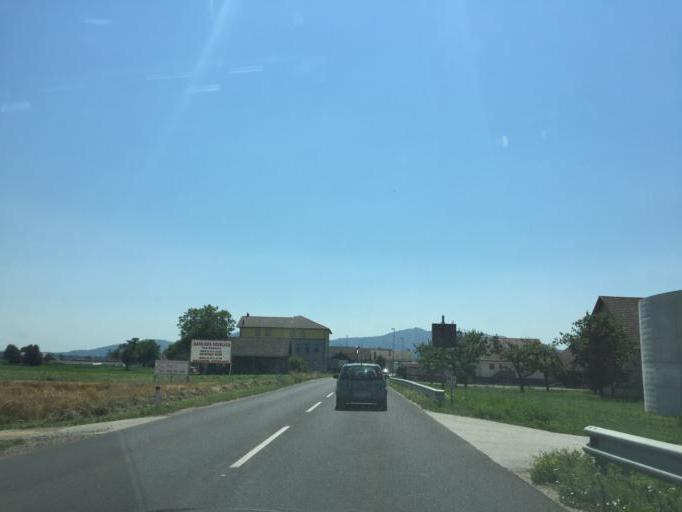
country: SI
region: Skofja Loka
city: Sv. Duh
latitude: 46.1990
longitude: 14.3322
